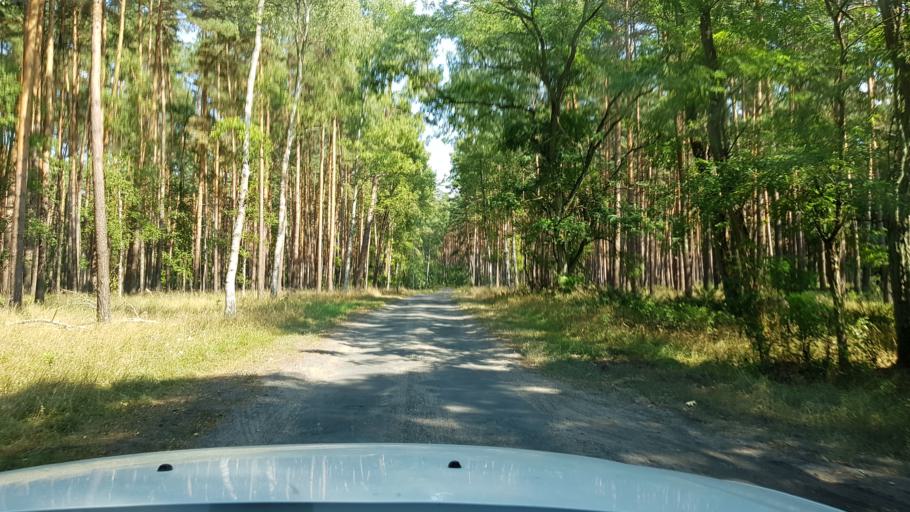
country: PL
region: West Pomeranian Voivodeship
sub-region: Powiat gryfinski
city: Moryn
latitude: 52.8133
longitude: 14.3332
